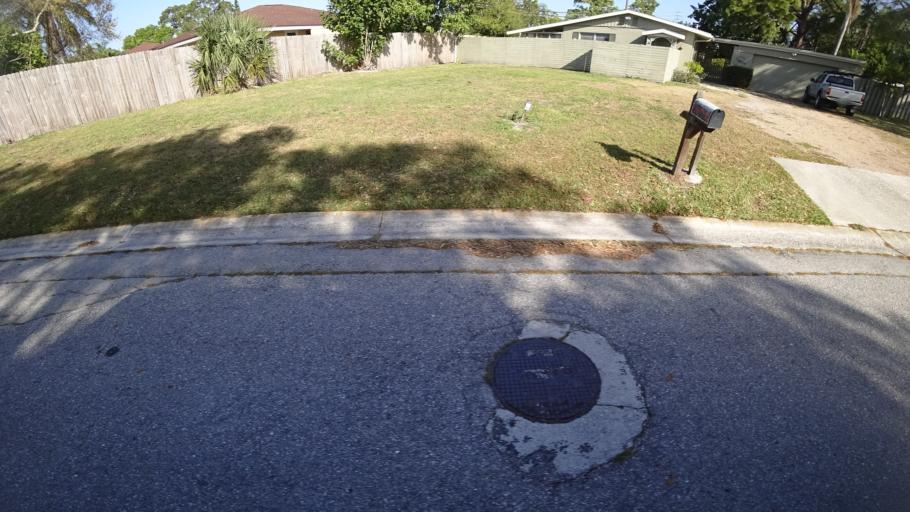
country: US
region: Florida
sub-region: Manatee County
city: Whitfield
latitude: 27.4175
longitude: -82.5581
